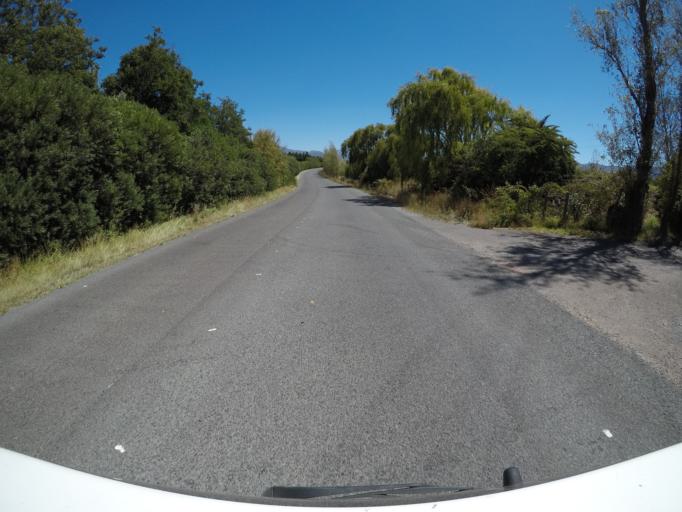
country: ZA
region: Western Cape
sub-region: Overberg District Municipality
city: Grabouw
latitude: -34.1872
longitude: 19.0395
